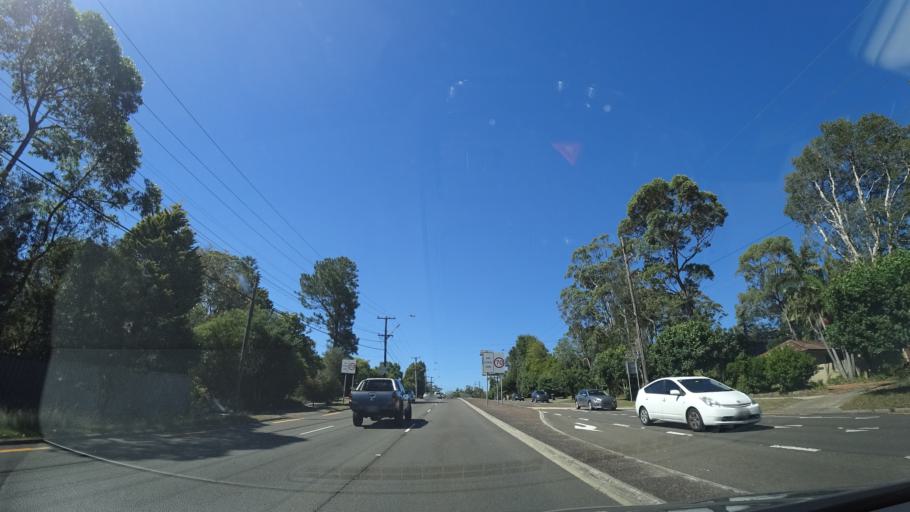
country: AU
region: New South Wales
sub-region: Warringah
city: Forestville
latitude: -33.7578
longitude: 151.2199
